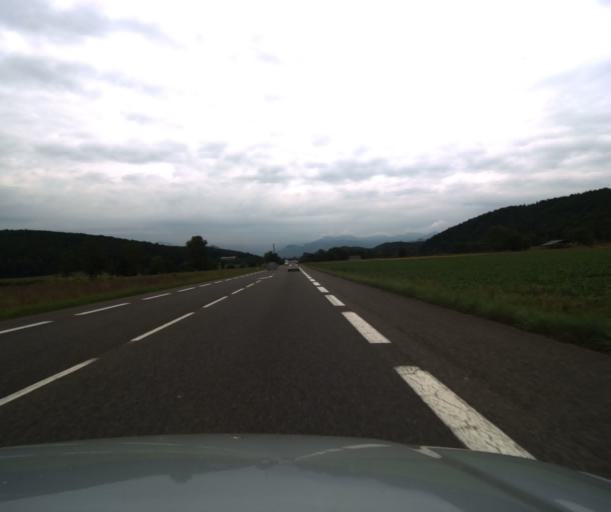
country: FR
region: Midi-Pyrenees
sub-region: Departement des Hautes-Pyrenees
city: Ossun
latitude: 43.1539
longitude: -0.0213
